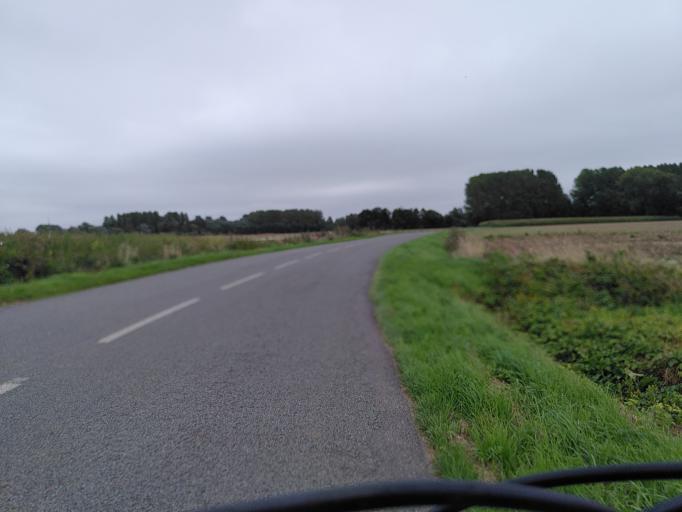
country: FR
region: Nord-Pas-de-Calais
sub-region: Departement du Pas-de-Calais
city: Aire-sur-la-Lys
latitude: 50.6487
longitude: 2.3749
